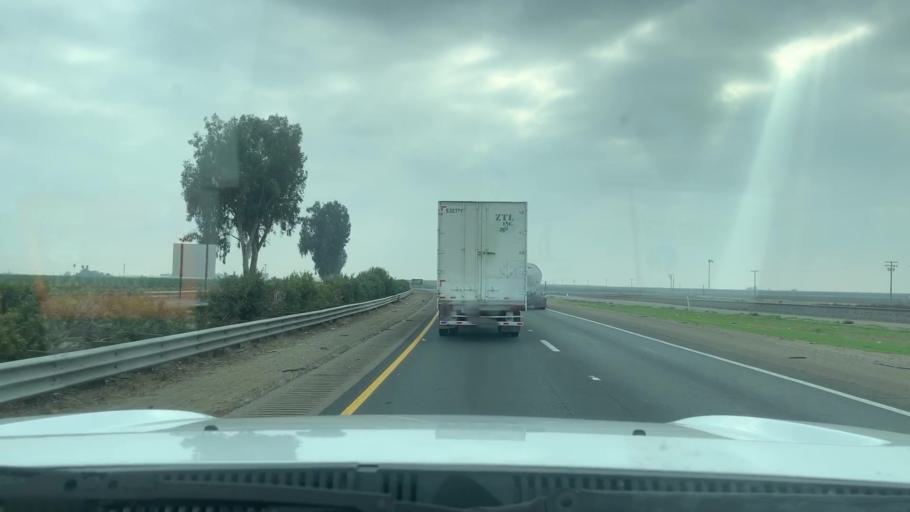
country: US
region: California
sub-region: Tulare County
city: Tipton
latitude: 36.0478
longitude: -119.3115
